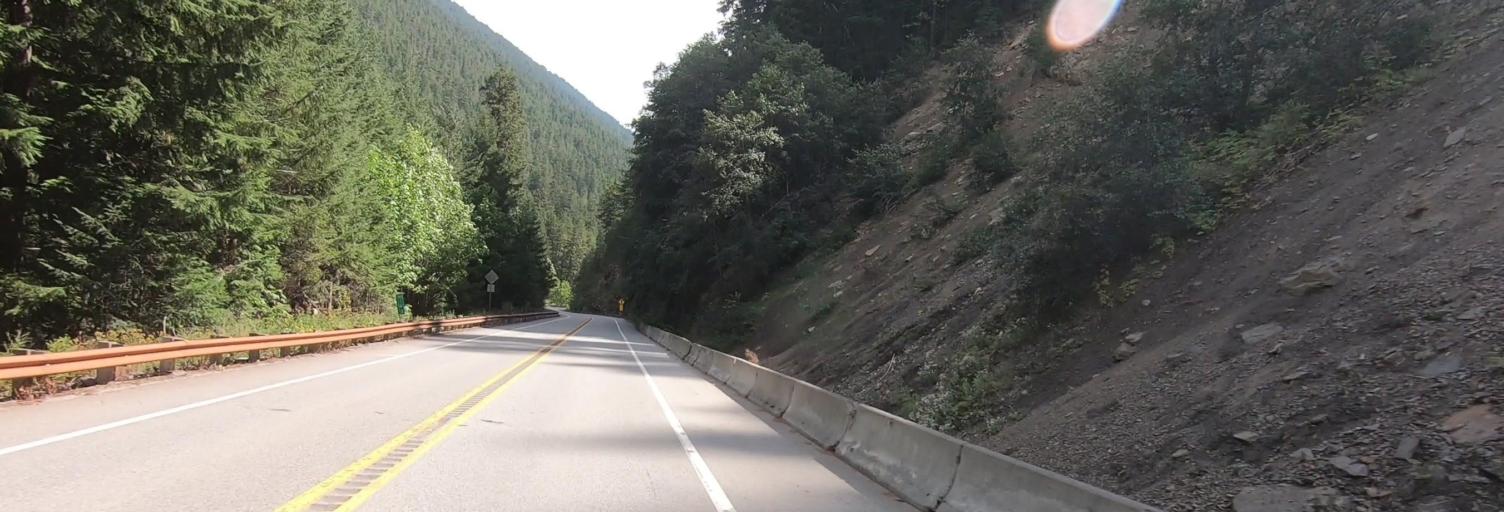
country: US
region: Washington
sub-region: Snohomish County
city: Darrington
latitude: 48.6962
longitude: -120.9115
